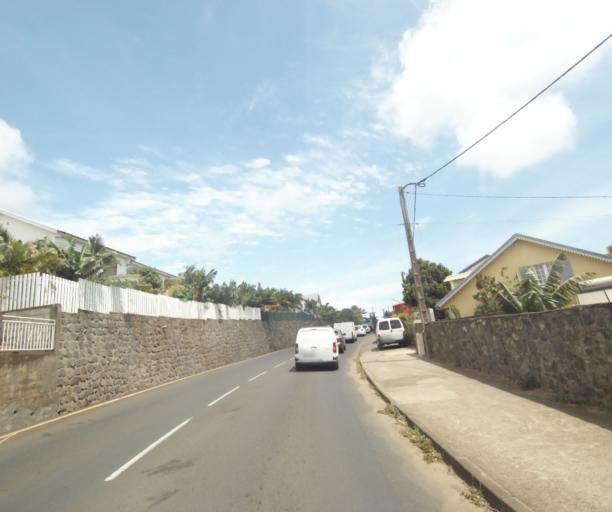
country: RE
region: Reunion
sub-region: Reunion
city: Trois-Bassins
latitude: -21.0727
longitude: 55.2676
